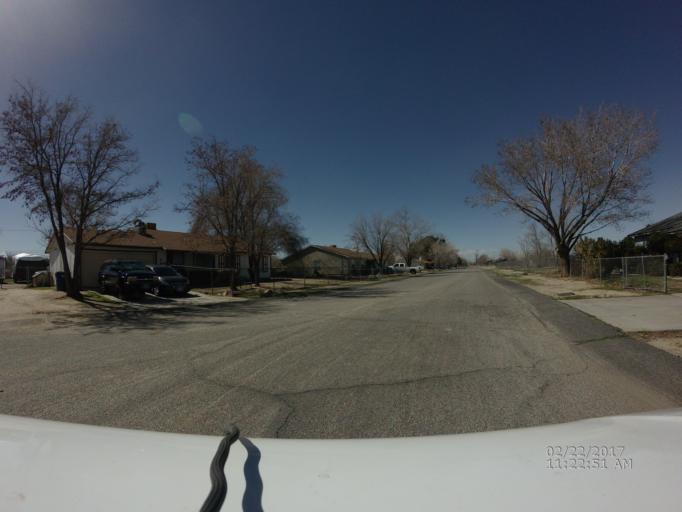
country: US
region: California
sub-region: Los Angeles County
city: Lake Los Angeles
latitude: 34.6176
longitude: -117.8109
